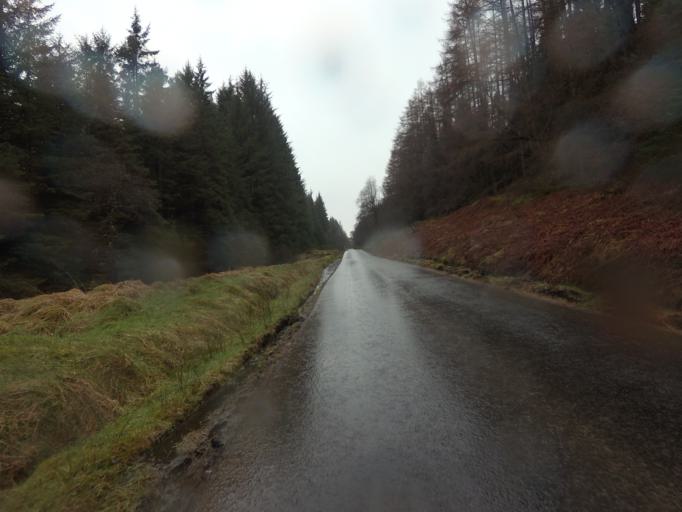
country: GB
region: Scotland
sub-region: West Dunbartonshire
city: Balloch
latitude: 56.2295
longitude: -4.5565
